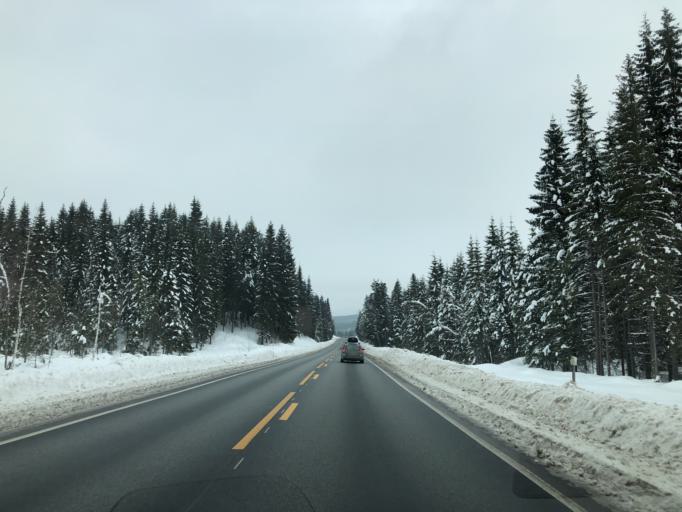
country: NO
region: Hedmark
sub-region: Elverum
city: Elverum
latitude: 60.9408
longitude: 11.6825
